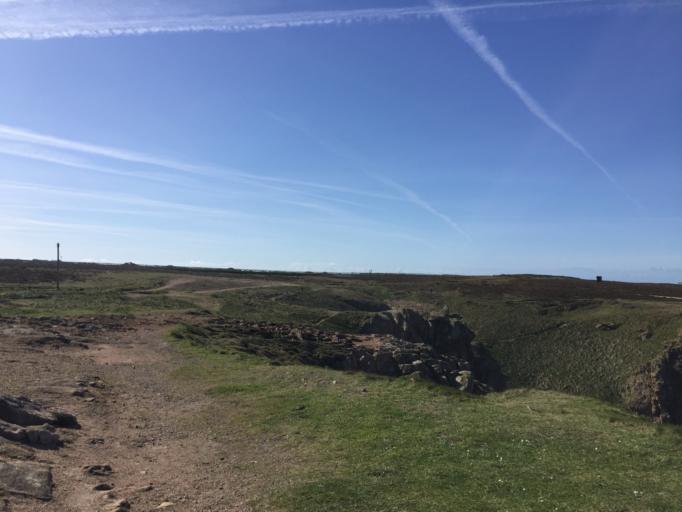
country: JE
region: St Helier
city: Saint Helier
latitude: 49.2572
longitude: -2.2463
